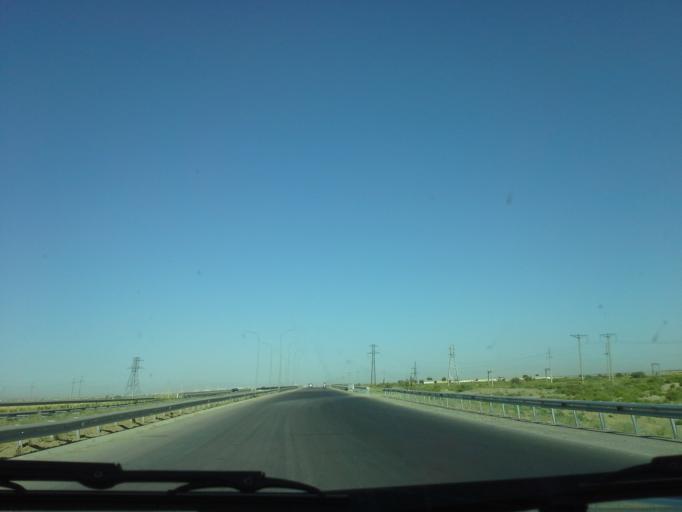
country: TM
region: Balkan
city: Gazanjyk
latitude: 39.2521
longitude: 55.5944
